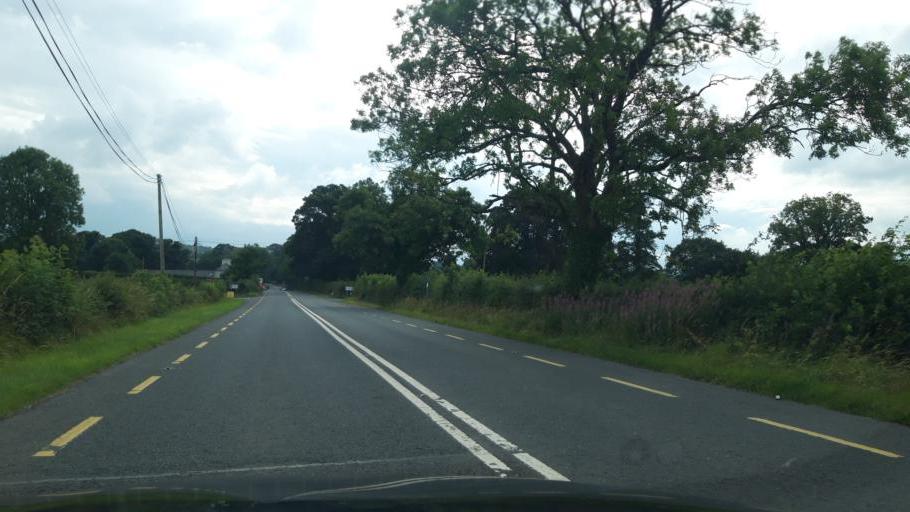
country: IE
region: Leinster
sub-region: Kilkenny
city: Castlecomer
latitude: 52.8482
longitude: -7.1243
